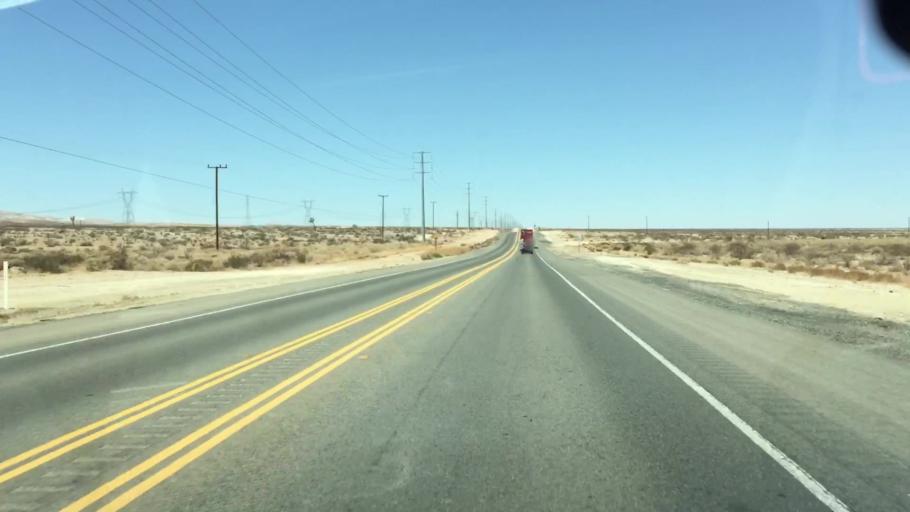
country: US
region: California
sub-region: San Bernardino County
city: Adelanto
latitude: 34.6551
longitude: -117.4380
